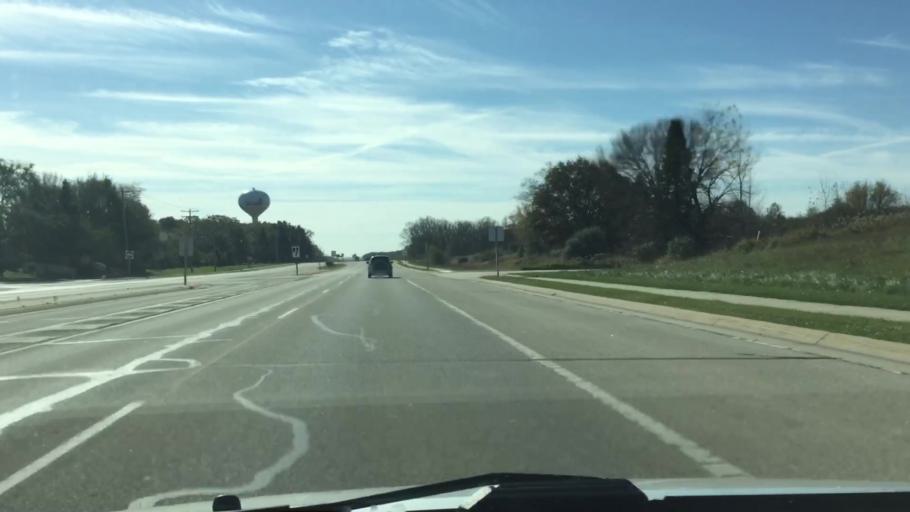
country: US
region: Wisconsin
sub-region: Waukesha County
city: Sussex
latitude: 43.1238
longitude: -88.2444
